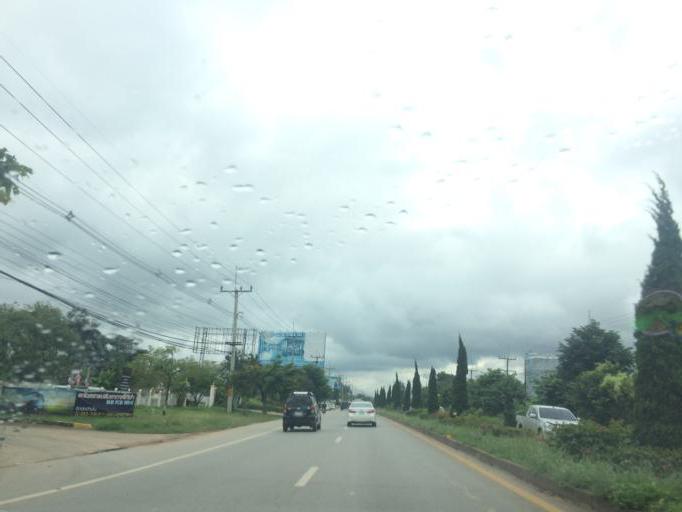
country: TH
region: Chiang Rai
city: Chiang Rai
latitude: 20.0112
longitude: 99.8686
